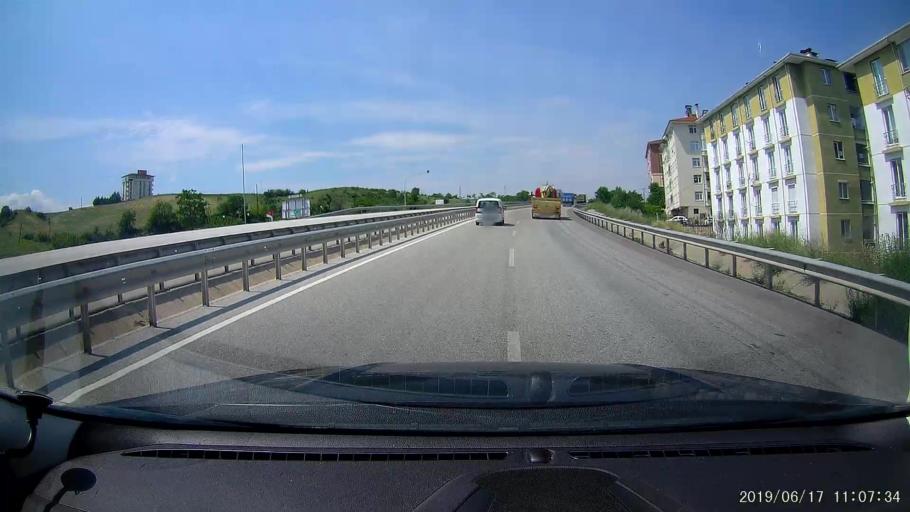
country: TR
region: Kastamonu
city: Tosya
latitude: 41.0010
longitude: 34.0533
